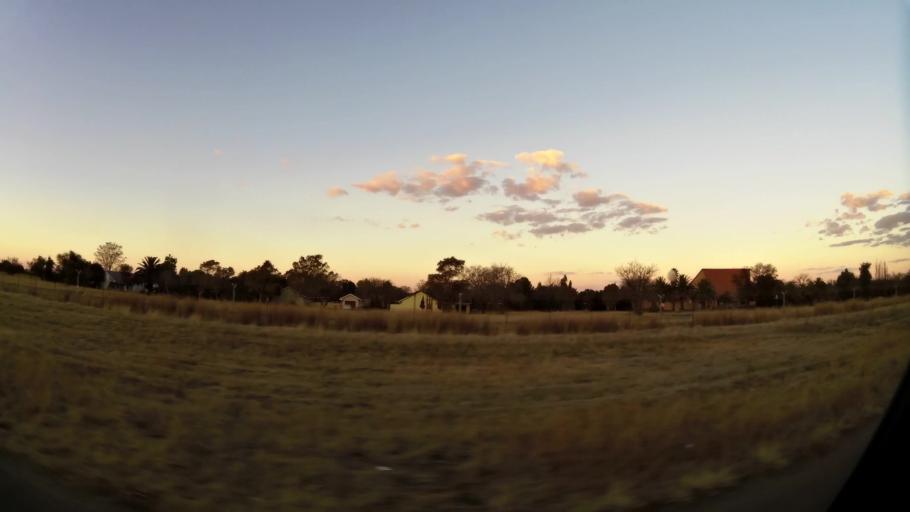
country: ZA
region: North-West
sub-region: Dr Kenneth Kaunda District Municipality
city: Potchefstroom
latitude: -26.6794
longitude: 27.0748
